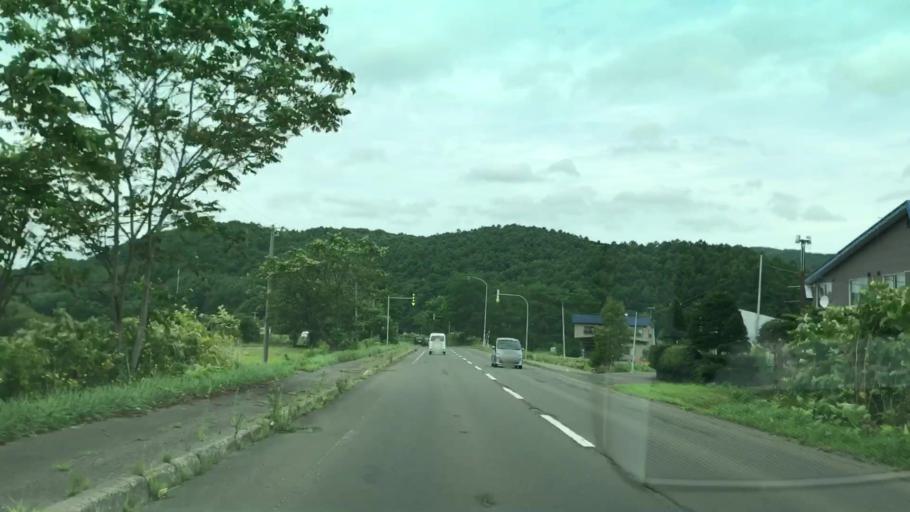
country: JP
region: Hokkaido
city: Iwanai
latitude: 42.9628
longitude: 140.6927
